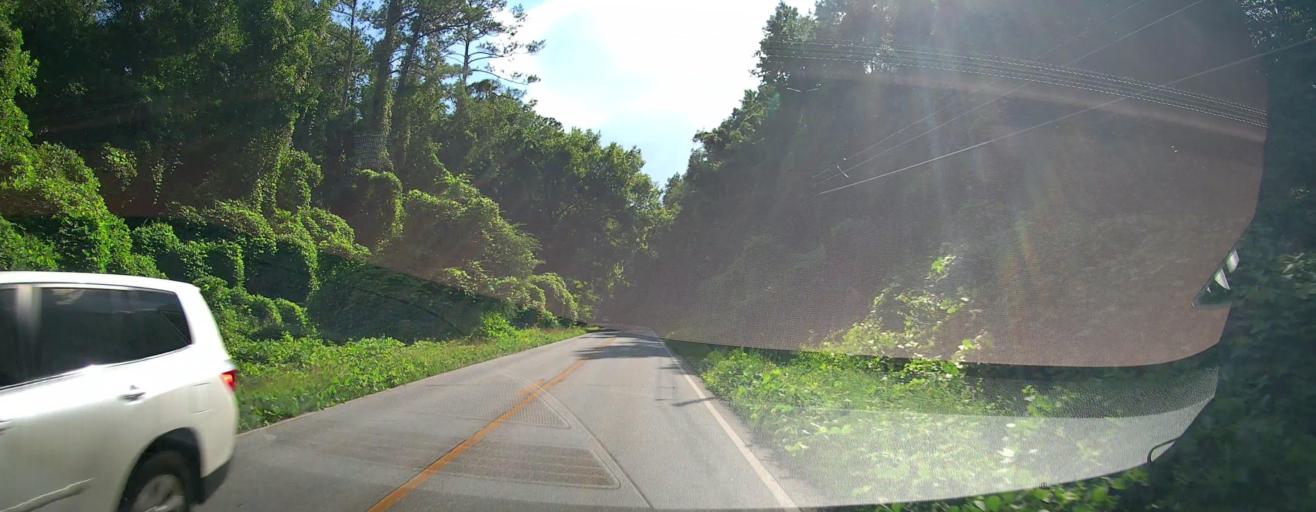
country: US
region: Georgia
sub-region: Muscogee County
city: Columbus
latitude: 32.5628
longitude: -84.8583
